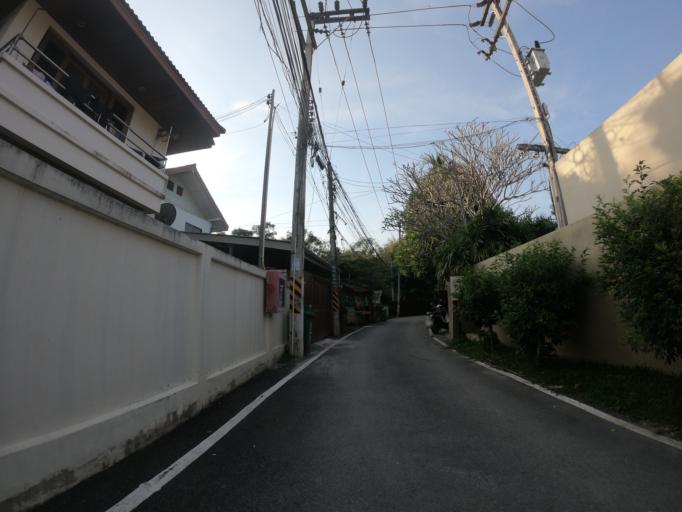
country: TH
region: Chiang Mai
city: Chiang Mai
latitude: 18.8184
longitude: 98.9552
